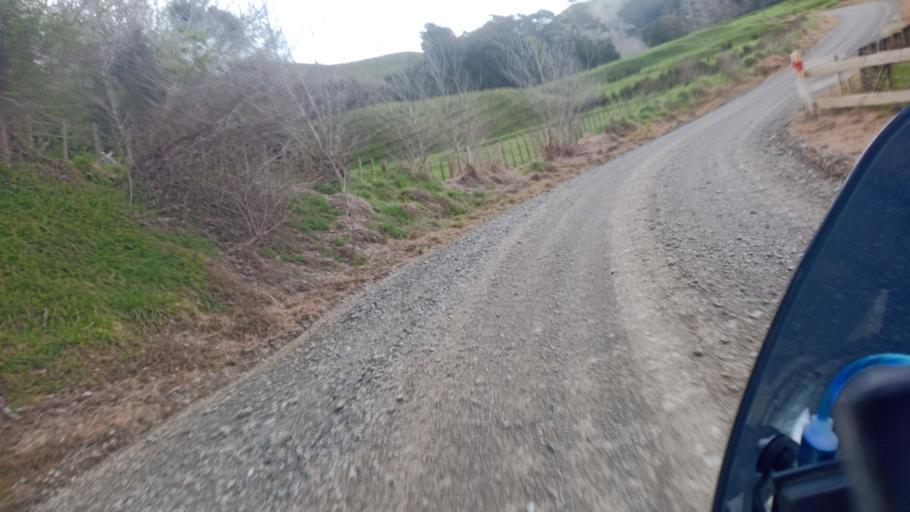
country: NZ
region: Gisborne
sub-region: Gisborne District
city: Gisborne
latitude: -38.2041
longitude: 178.2414
